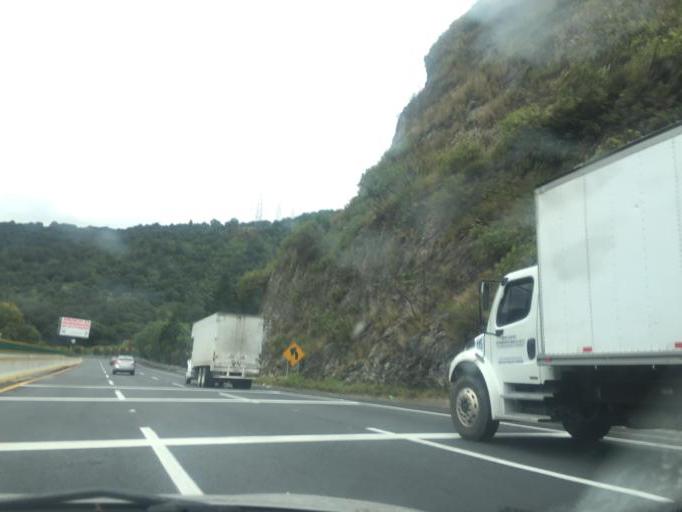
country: MX
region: Mexico City
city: Xochimilco
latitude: 19.2271
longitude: -99.1452
